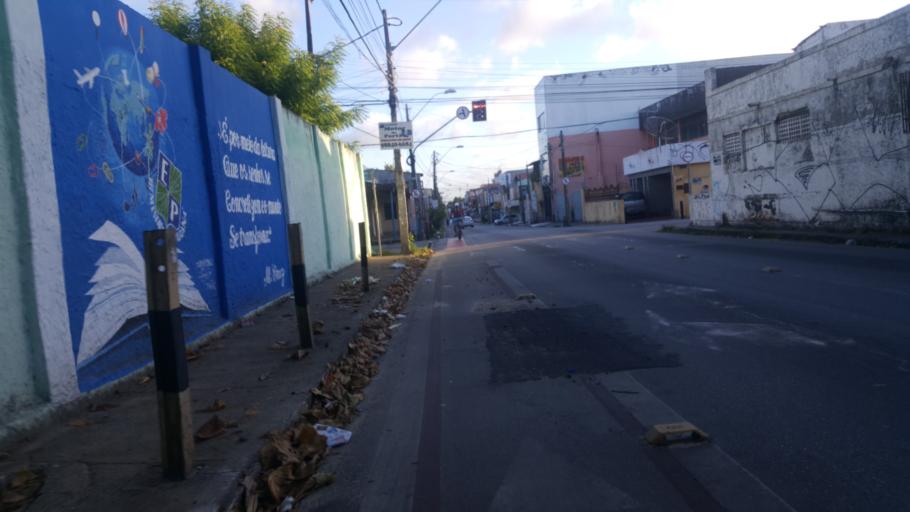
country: BR
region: Ceara
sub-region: Fortaleza
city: Fortaleza
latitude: -3.7573
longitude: -38.5434
